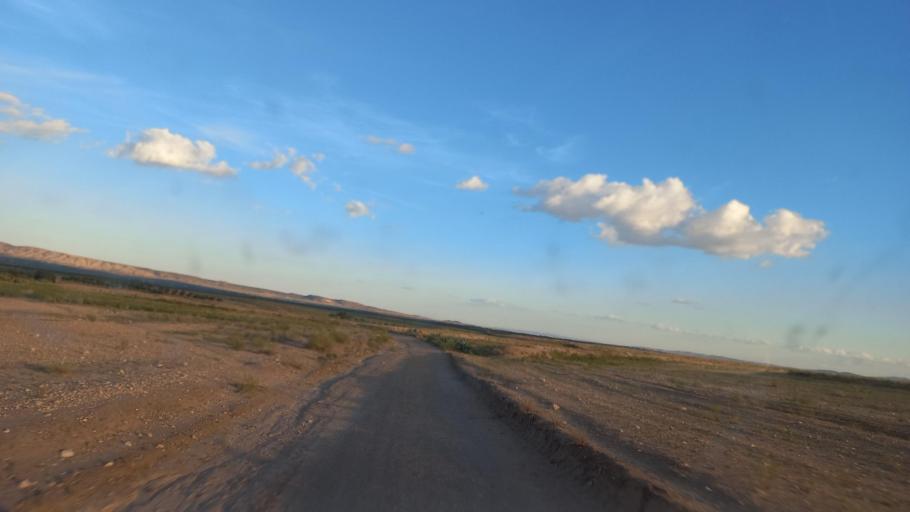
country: TN
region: Al Qasrayn
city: Sbiba
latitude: 35.3501
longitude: 9.0226
